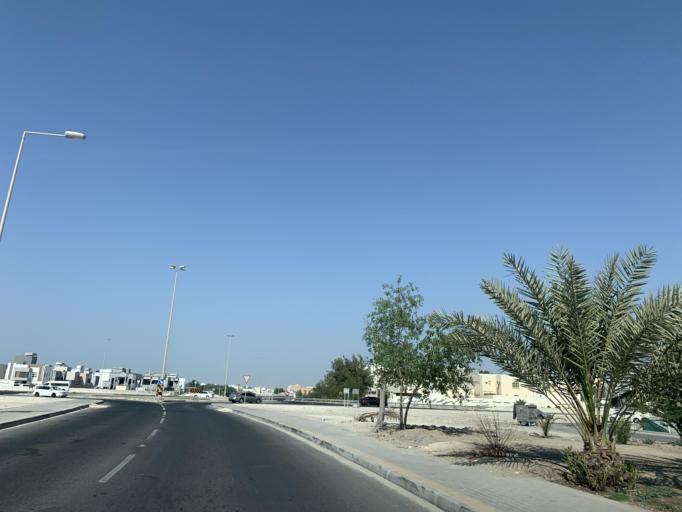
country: BH
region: Central Governorate
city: Dar Kulayb
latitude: 26.0825
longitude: 50.5024
